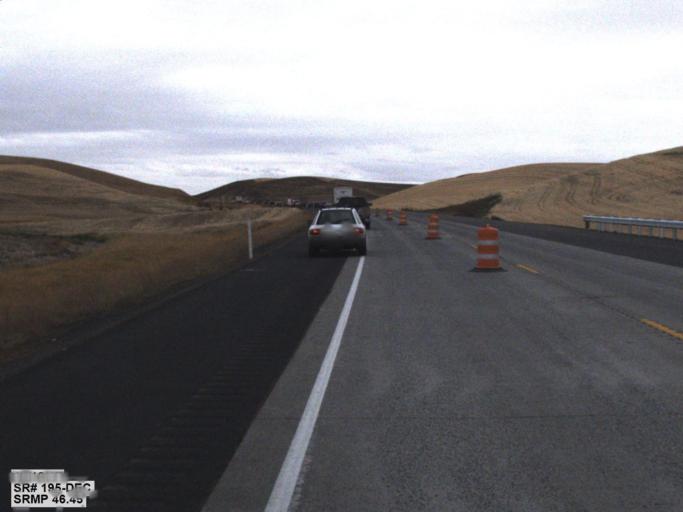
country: US
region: Washington
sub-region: Whitman County
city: Colfax
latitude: 46.9847
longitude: -117.3471
